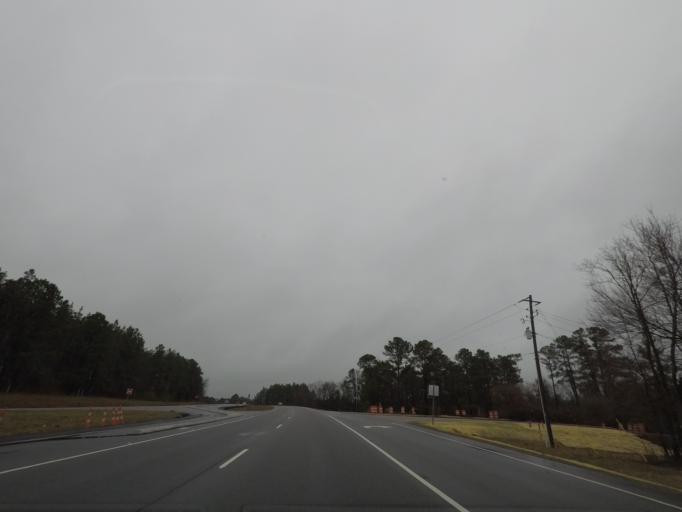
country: US
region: North Carolina
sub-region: Lee County
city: Broadway
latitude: 35.3322
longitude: -79.0942
